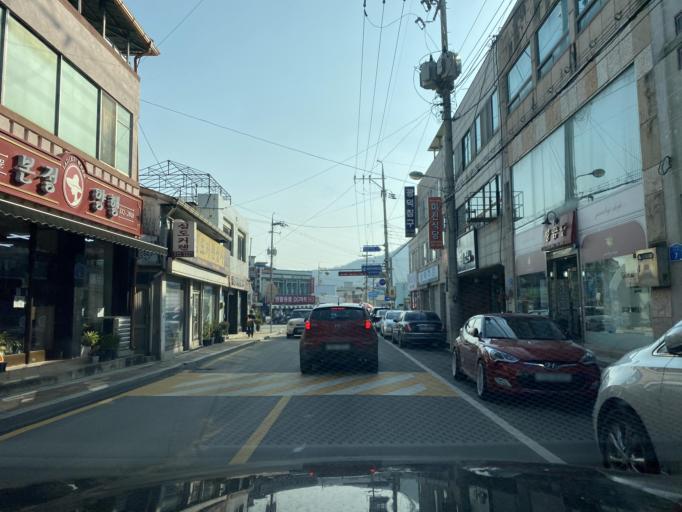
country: KR
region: Chungcheongnam-do
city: Yesan
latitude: 36.6788
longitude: 126.8497
